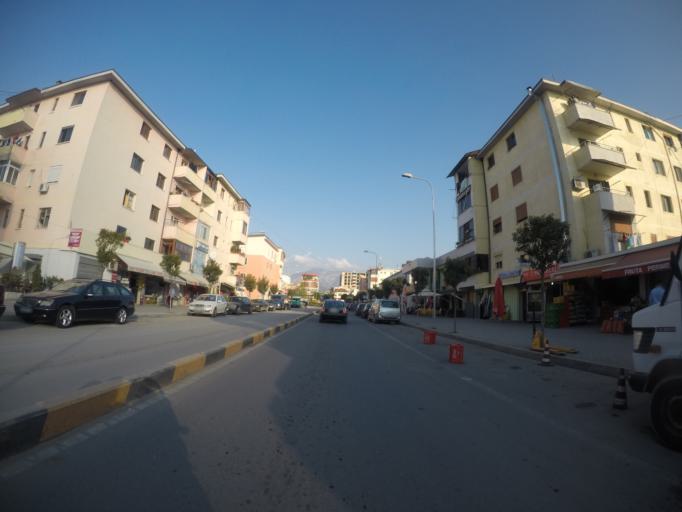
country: AL
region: Durres
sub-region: Rrethi i Krujes
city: Fushe-Kruje
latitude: 41.4792
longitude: 19.7192
